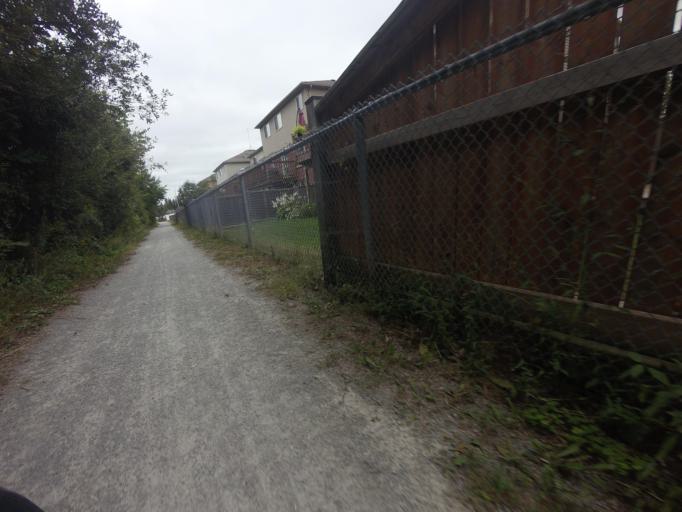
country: CA
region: Ontario
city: Omemee
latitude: 44.3366
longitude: -78.7504
